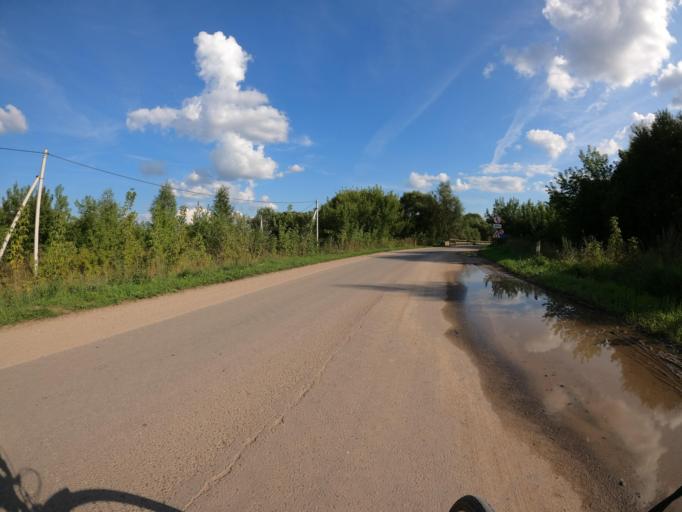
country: RU
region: Moskovskaya
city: Troitskoye
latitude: 55.1944
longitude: 38.4897
